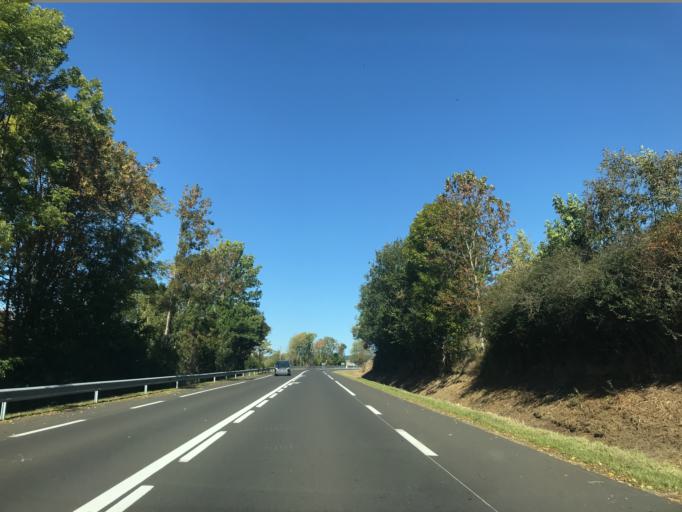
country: FR
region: Auvergne
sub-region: Departement du Puy-de-Dome
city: Gelles
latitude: 45.6937
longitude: 2.8057
